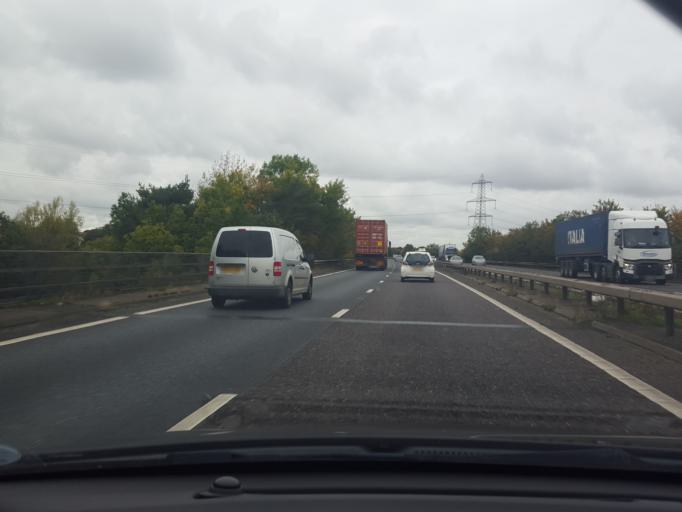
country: GB
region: England
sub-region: Suffolk
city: Needham Market
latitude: 52.1460
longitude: 1.0795
